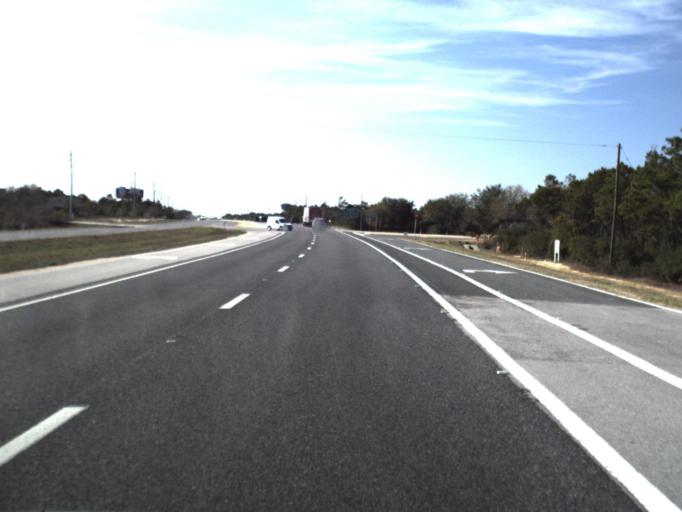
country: US
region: Florida
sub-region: Bay County
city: Laguna Beach
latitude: 30.2610
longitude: -85.9545
